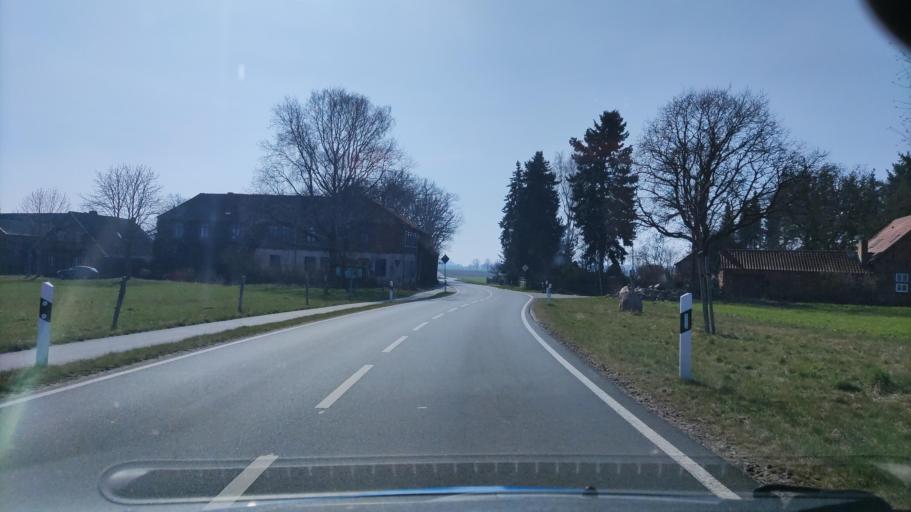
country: DE
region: Lower Saxony
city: Waddeweitz
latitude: 52.9679
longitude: 10.9714
